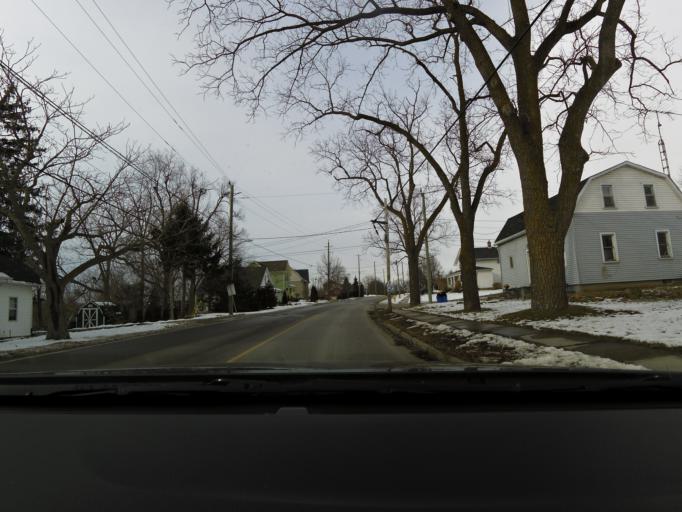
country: CA
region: Ontario
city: Ancaster
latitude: 43.0676
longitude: -79.9383
